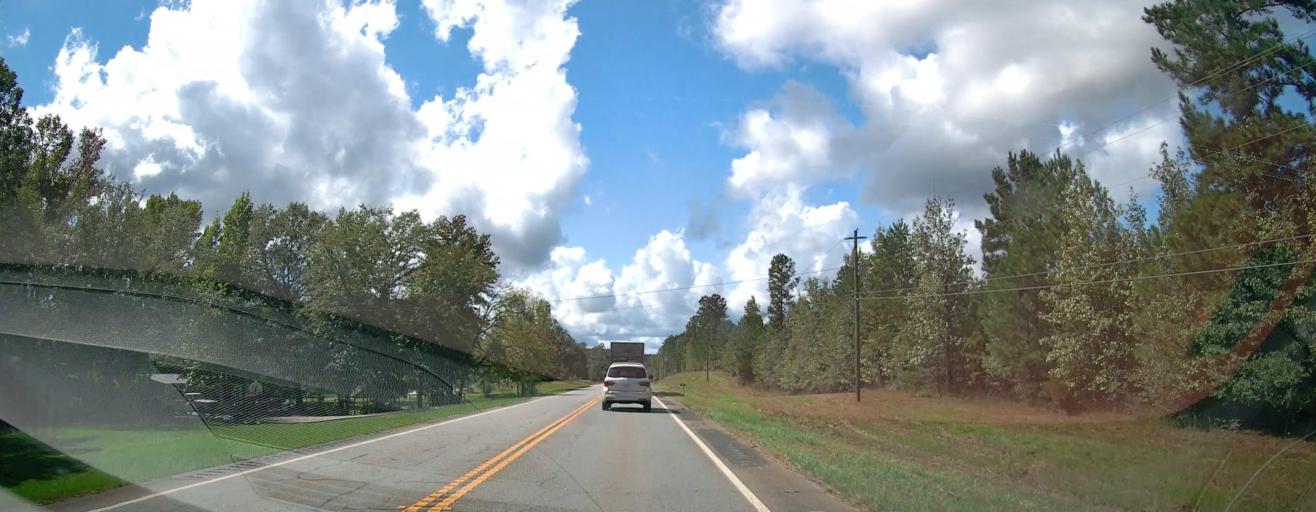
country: US
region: Georgia
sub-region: Jones County
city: Gray
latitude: 33.0279
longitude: -83.4594
